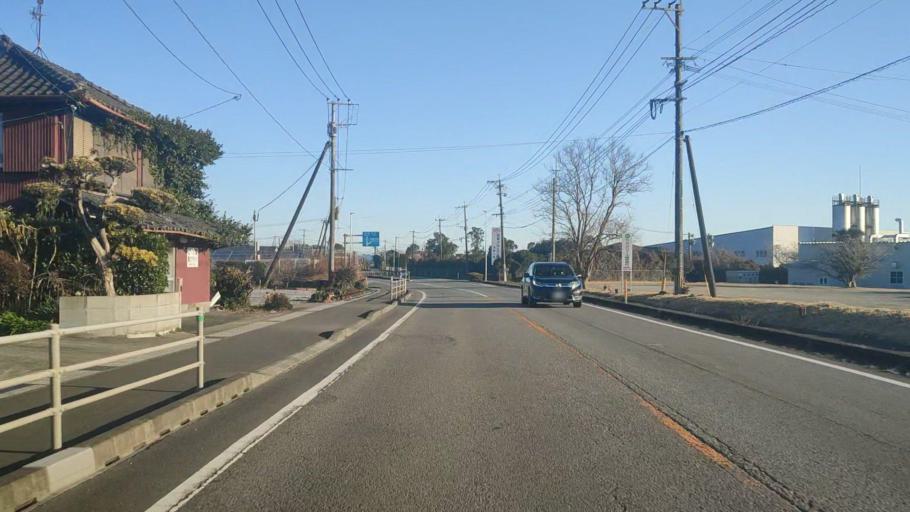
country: JP
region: Miyazaki
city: Takanabe
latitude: 32.2436
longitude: 131.5506
